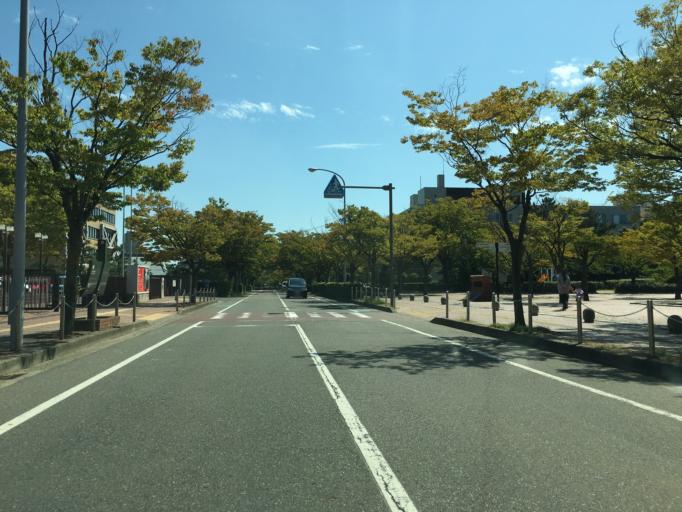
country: JP
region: Niigata
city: Niigata-shi
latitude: 37.9280
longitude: 139.0416
